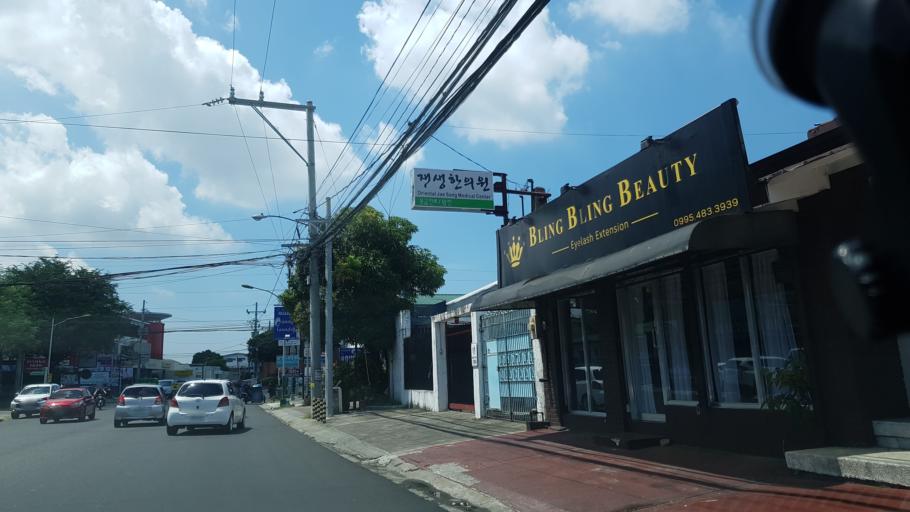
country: PH
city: Sambayanihan People's Village
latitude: 14.4455
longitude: 121.0226
